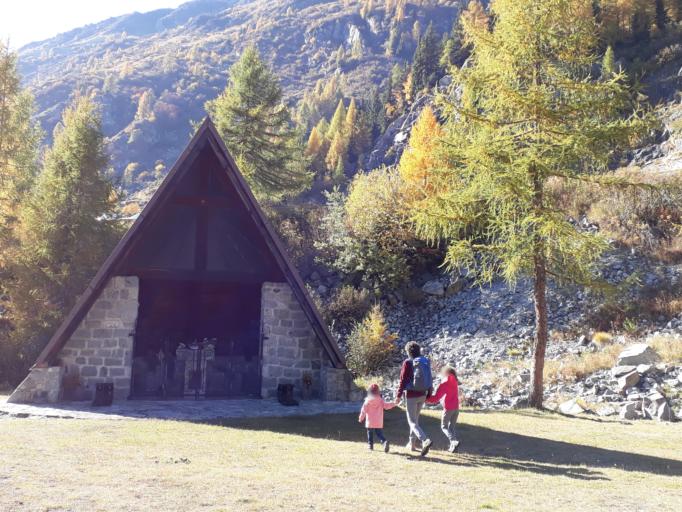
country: IT
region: Lombardy
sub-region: Provincia di Brescia
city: Saviore
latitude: 46.0512
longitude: 10.5118
